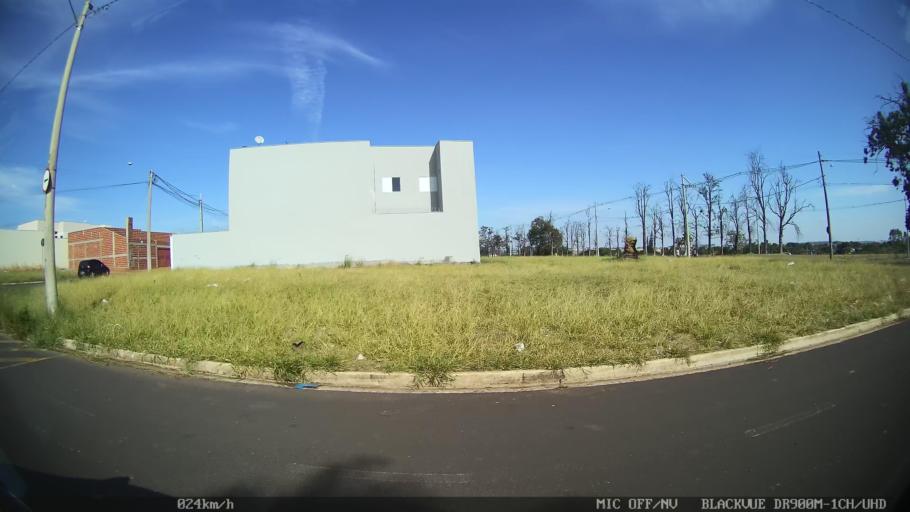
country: BR
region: Sao Paulo
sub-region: Franca
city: Franca
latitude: -20.5066
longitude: -47.4411
